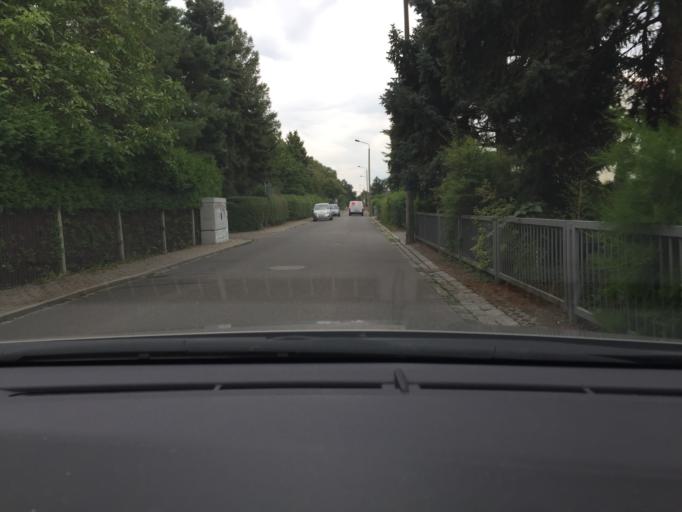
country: DE
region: Saxony
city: Taucha
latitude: 51.3846
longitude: 12.4630
